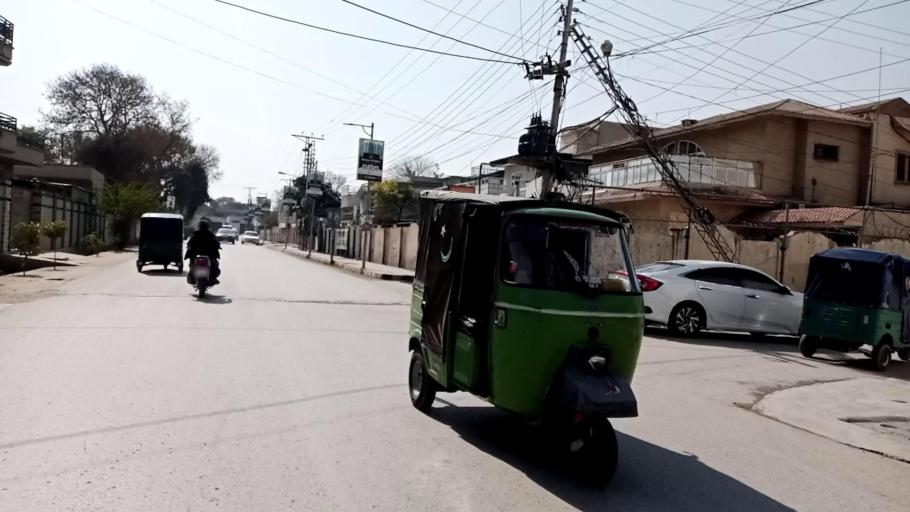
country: PK
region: Khyber Pakhtunkhwa
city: Peshawar
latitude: 33.9992
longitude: 71.5002
